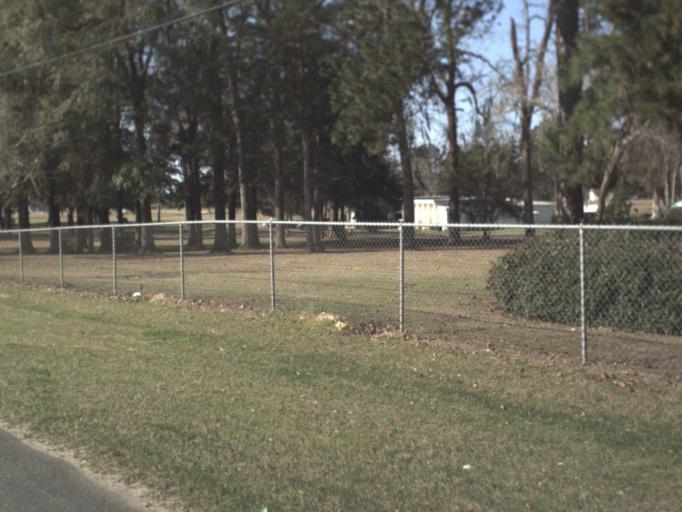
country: US
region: Florida
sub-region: Jackson County
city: Marianna
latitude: 30.8293
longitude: -85.1677
